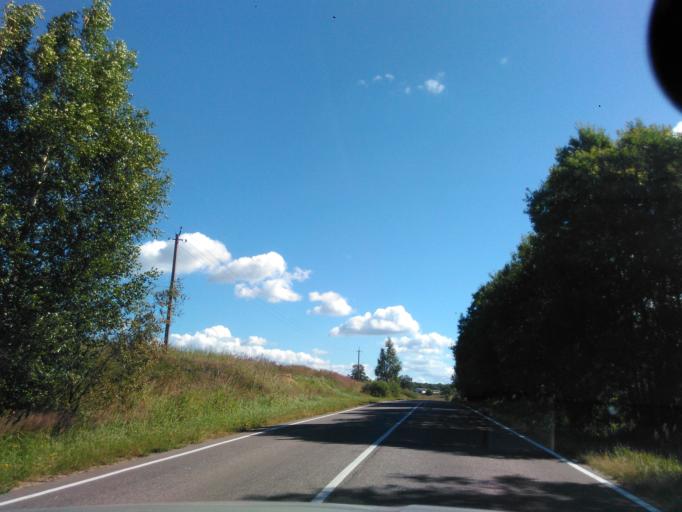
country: RU
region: Moskovskaya
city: Klin
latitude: 56.1820
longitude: 36.8022
